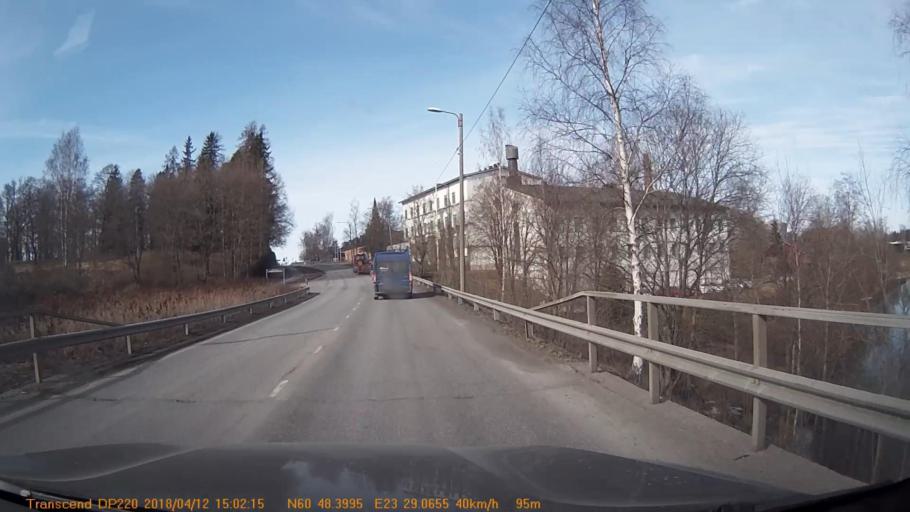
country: FI
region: Haeme
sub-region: Forssa
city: Jokioinen
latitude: 60.8068
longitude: 23.4844
